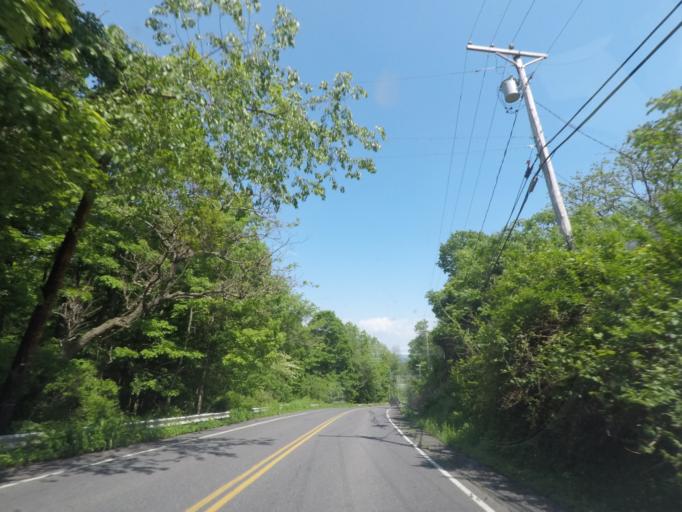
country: US
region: New York
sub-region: Dutchess County
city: Pine Plains
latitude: 41.9679
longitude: -73.5346
